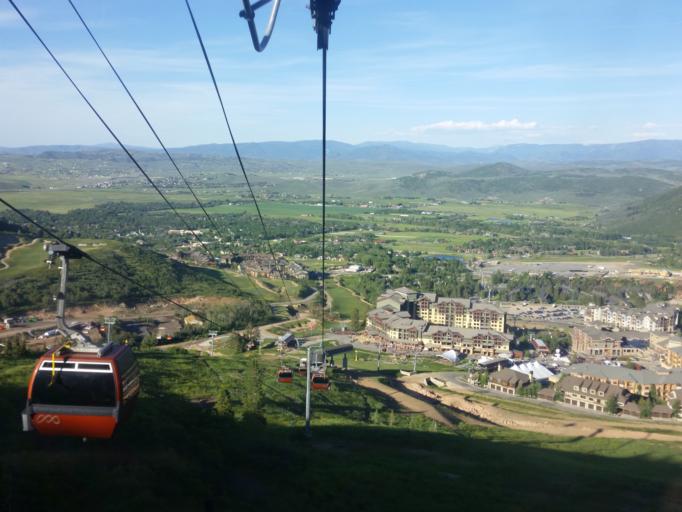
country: US
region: Utah
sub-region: Summit County
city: Snyderville
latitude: 40.6845
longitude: -111.5624
